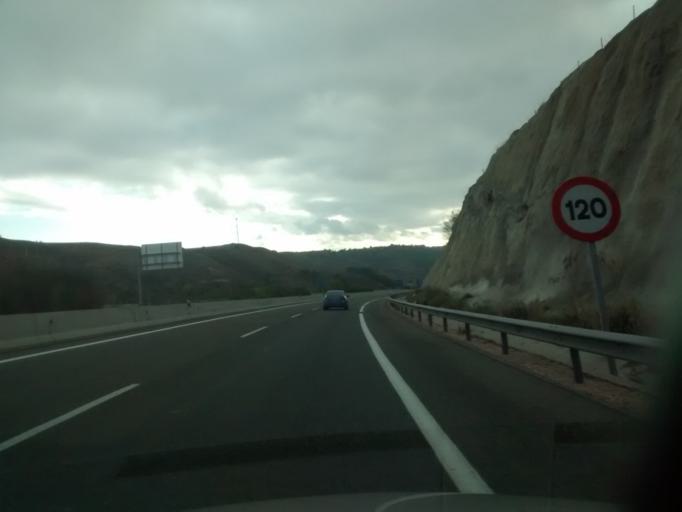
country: ES
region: Castille-La Mancha
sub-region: Provincia de Guadalajara
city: Torija
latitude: 40.7427
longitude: -3.0353
